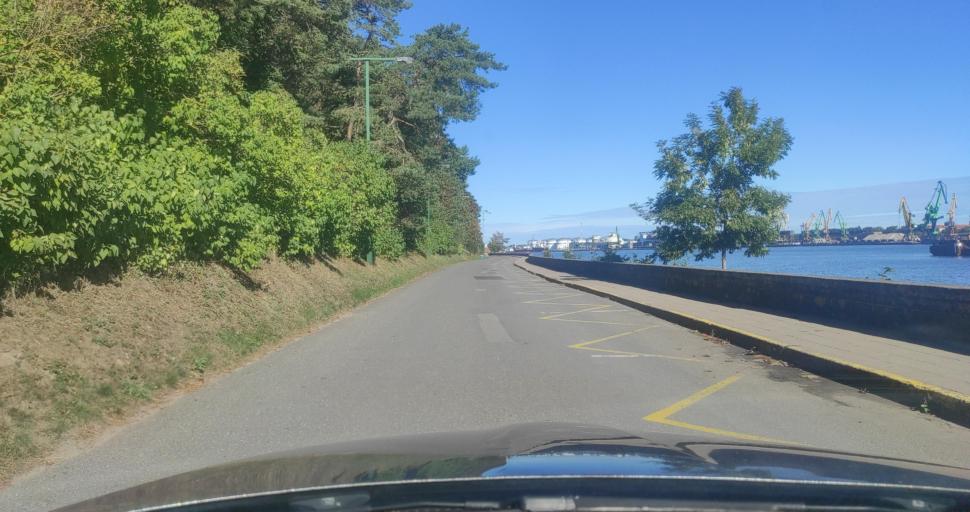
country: LT
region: Klaipedos apskritis
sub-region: Klaipeda
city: Klaipeda
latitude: 55.7090
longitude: 21.1102
